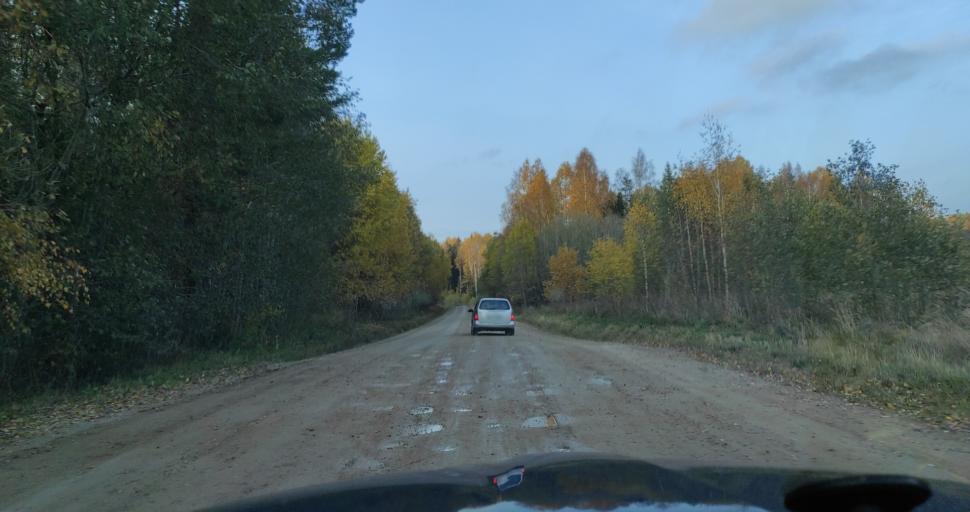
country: LV
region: Vainode
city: Vainode
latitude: 56.4674
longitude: 21.8597
